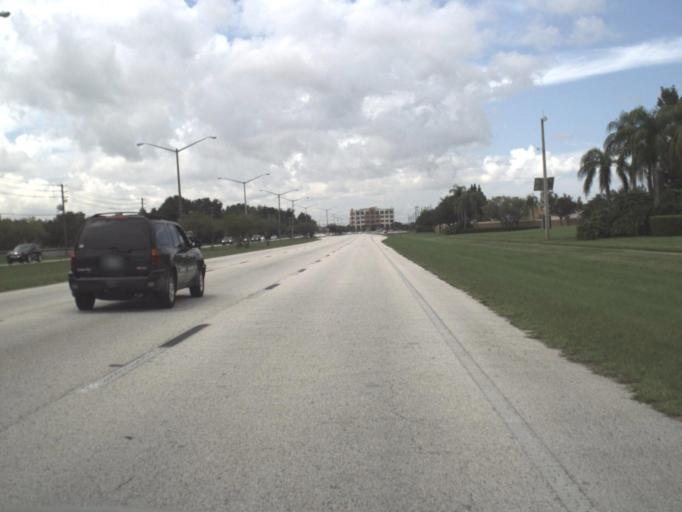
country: US
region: Florida
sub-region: Pinellas County
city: Saint George
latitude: 28.0749
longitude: -82.7040
